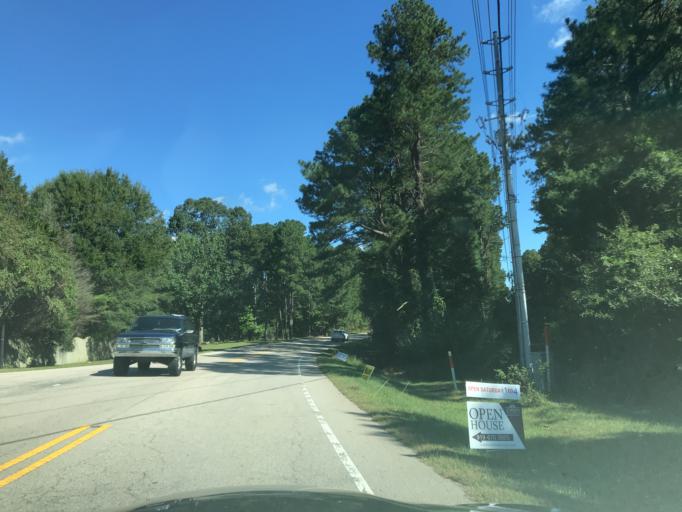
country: US
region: North Carolina
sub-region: Wake County
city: Wake Forest
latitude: 35.9238
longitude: -78.5168
